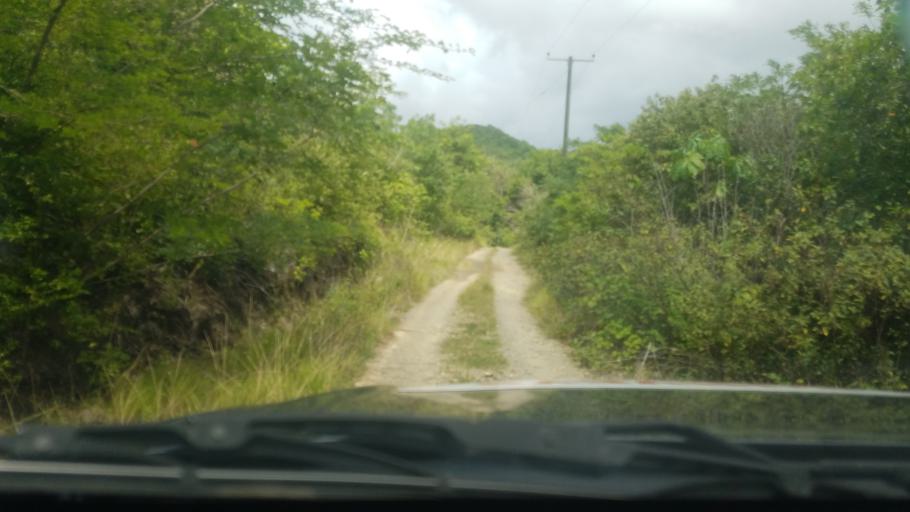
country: LC
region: Praslin
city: Praslin
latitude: 13.8689
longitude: -60.8967
